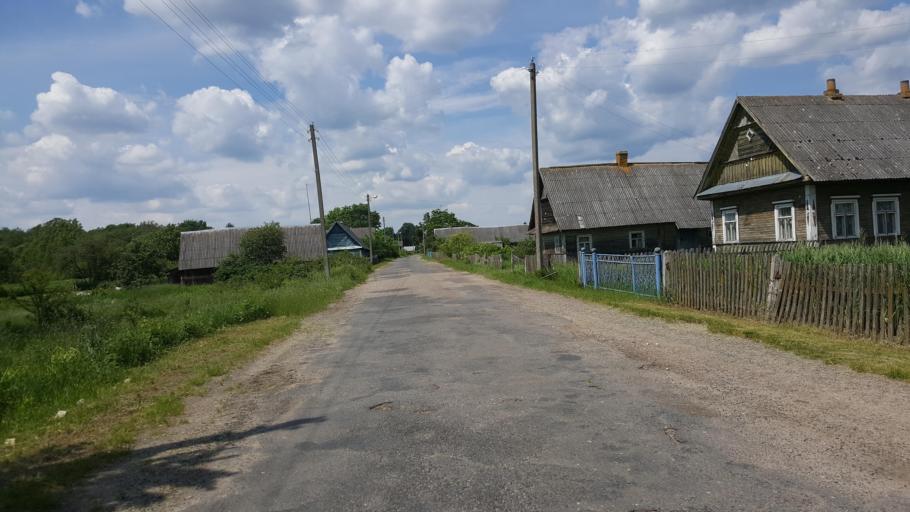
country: BY
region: Brest
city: Zhabinka
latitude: 52.4769
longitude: 24.1481
